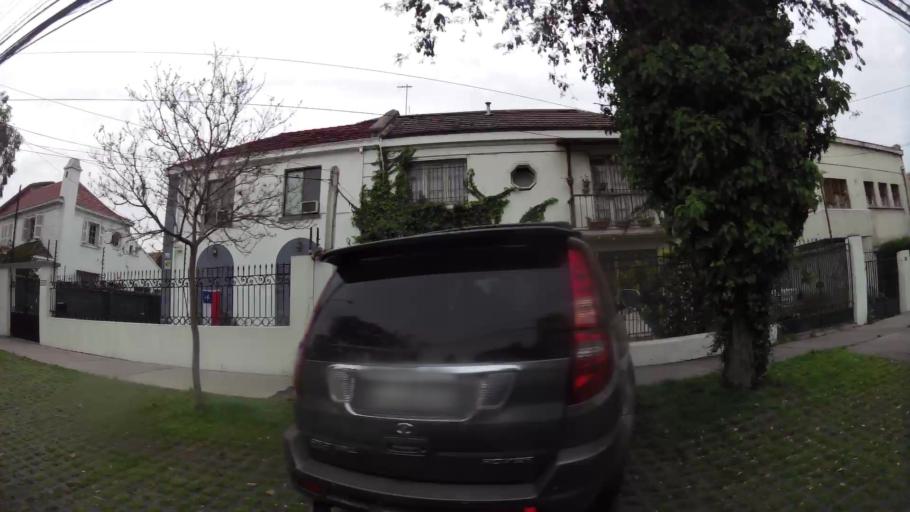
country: CL
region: Santiago Metropolitan
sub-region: Provincia de Santiago
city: Santiago
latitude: -33.4503
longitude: -70.6181
